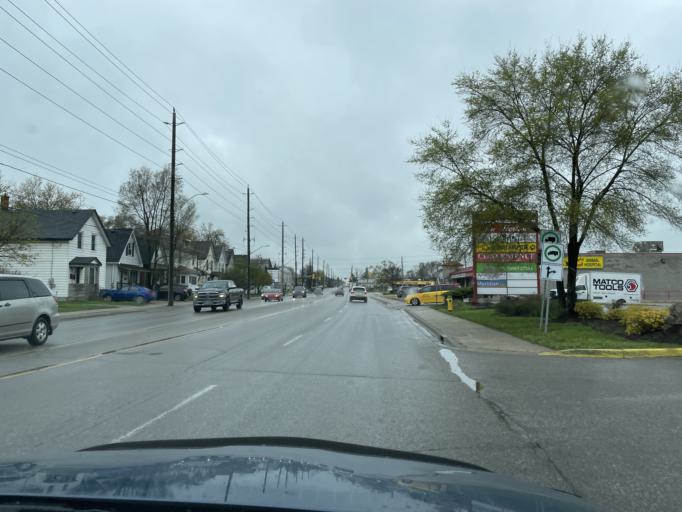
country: CA
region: Ontario
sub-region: Wellington County
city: Guelph
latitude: 43.5508
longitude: -80.2221
